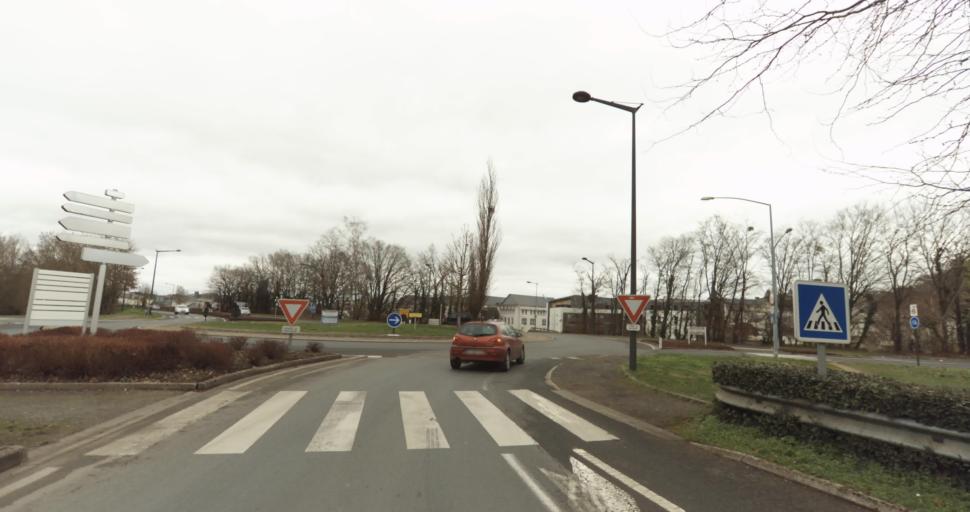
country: FR
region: Pays de la Loire
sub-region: Departement de Maine-et-Loire
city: Saumur
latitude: 47.2499
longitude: -0.0792
